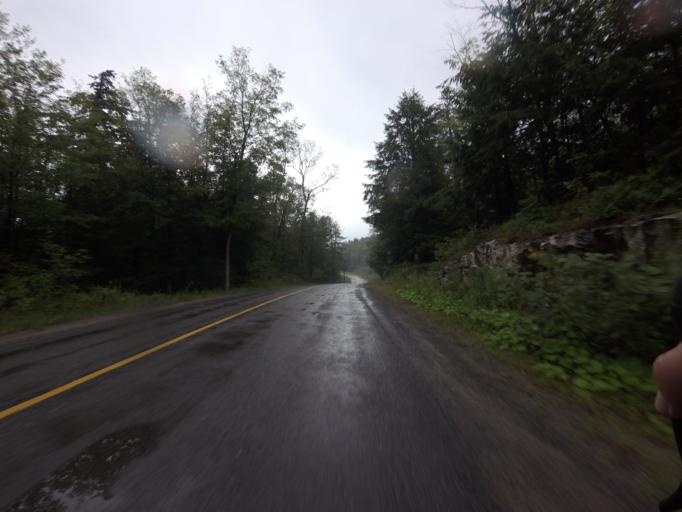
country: CA
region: Ontario
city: Perth
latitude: 45.0550
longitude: -76.5963
